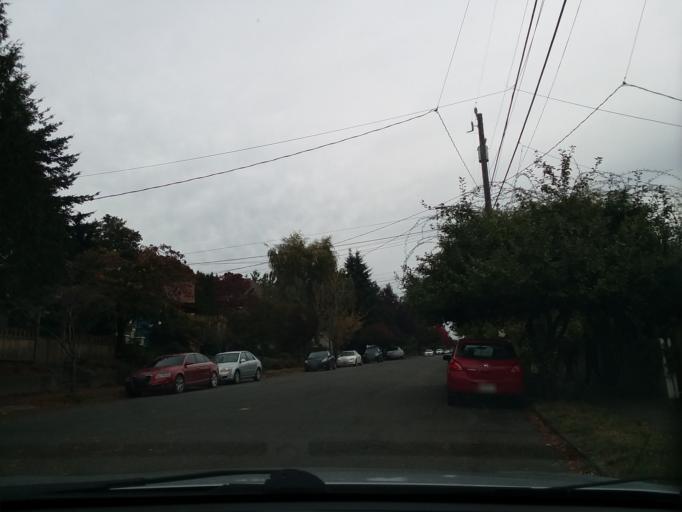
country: US
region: Washington
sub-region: King County
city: Seattle
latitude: 47.6567
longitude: -122.3446
